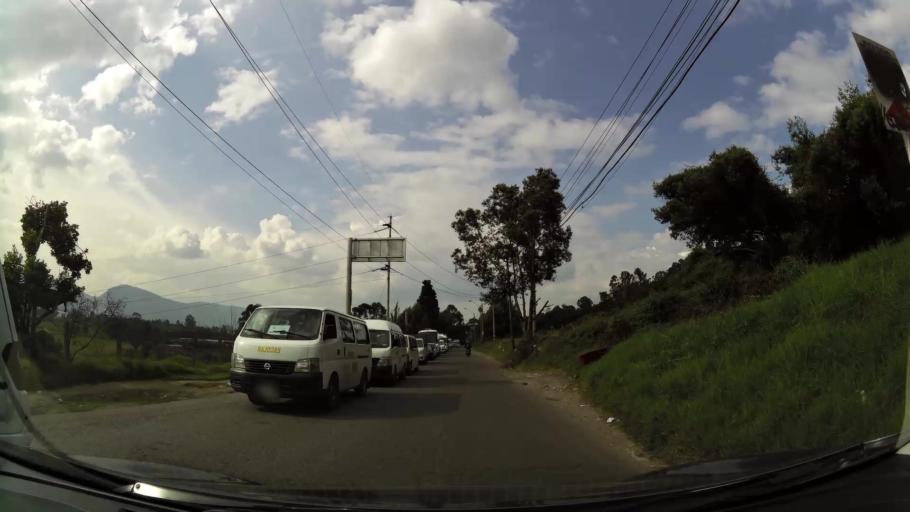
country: CO
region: Cundinamarca
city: Cota
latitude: 4.7607
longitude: -74.0771
